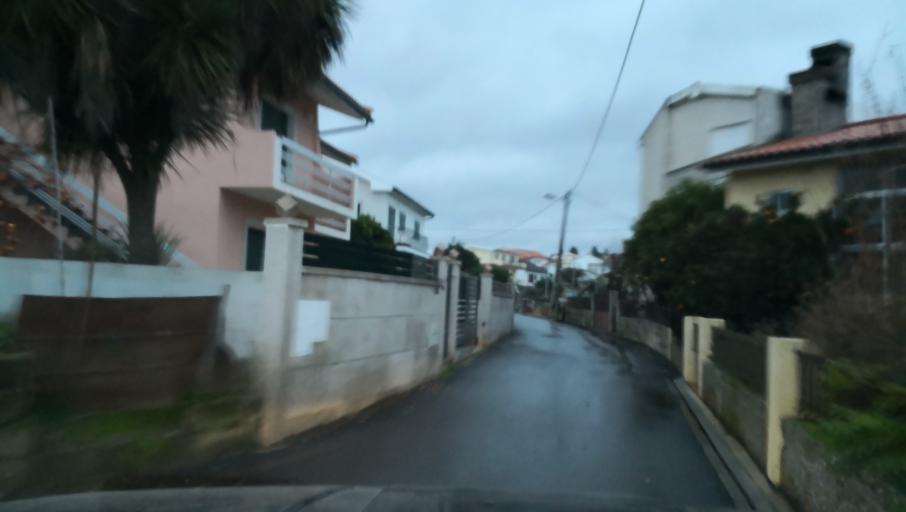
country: PT
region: Vila Real
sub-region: Vila Real
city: Vila Real
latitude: 41.2569
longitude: -7.7354
